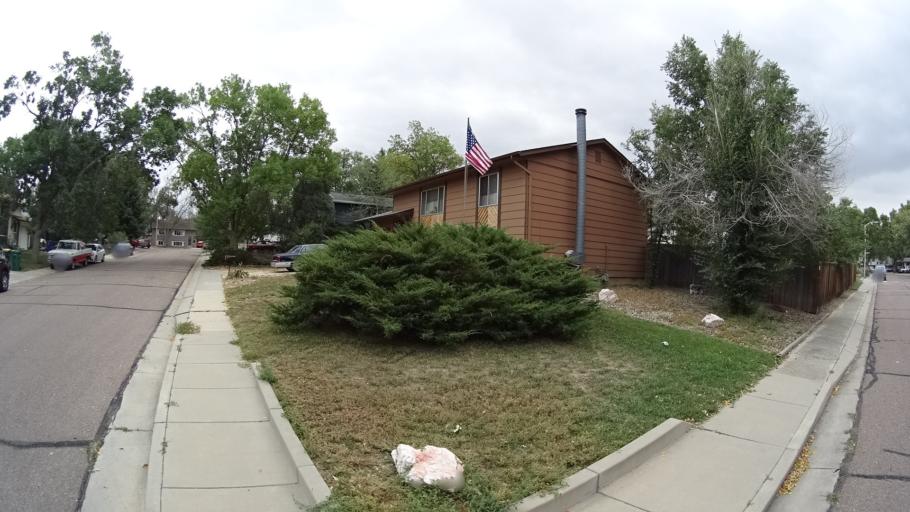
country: US
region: Colorado
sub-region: El Paso County
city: Cimarron Hills
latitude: 38.8907
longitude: -104.7422
